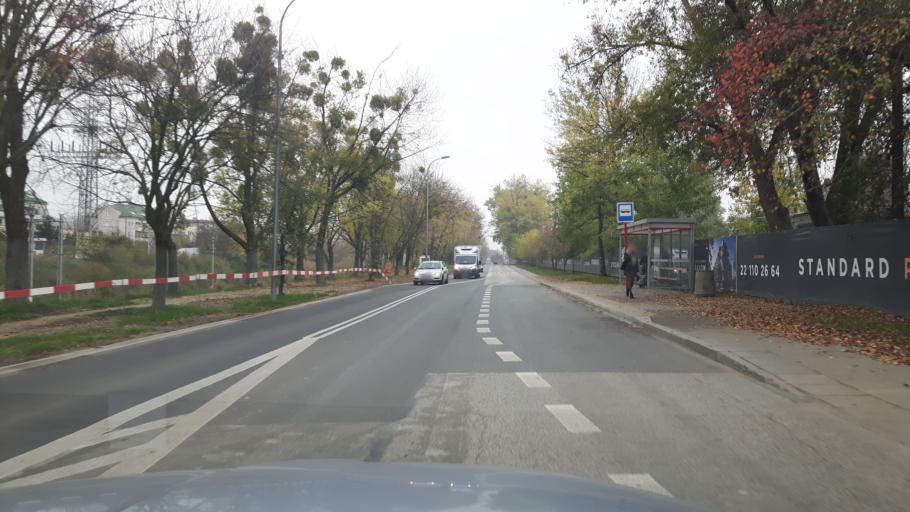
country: PL
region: Masovian Voivodeship
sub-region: Warszawa
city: Wlochy
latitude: 52.1991
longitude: 20.9543
